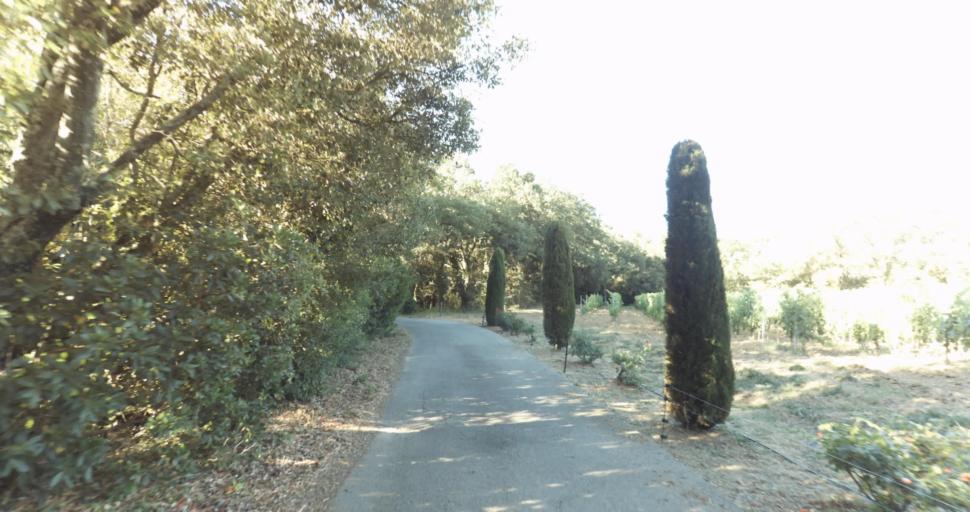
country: FR
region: Provence-Alpes-Cote d'Azur
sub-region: Departement du Var
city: Gassin
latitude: 43.2320
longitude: 6.5951
